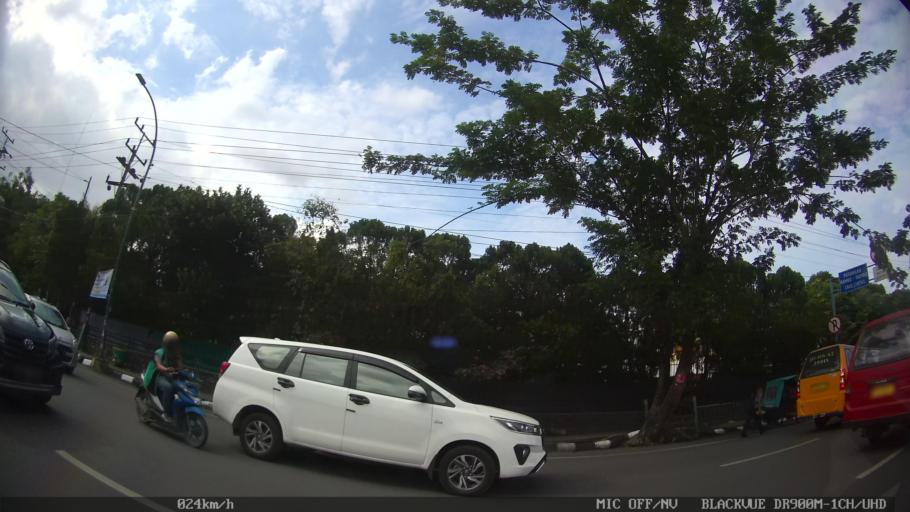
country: ID
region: North Sumatra
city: Medan
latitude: 3.5991
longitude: 98.6838
